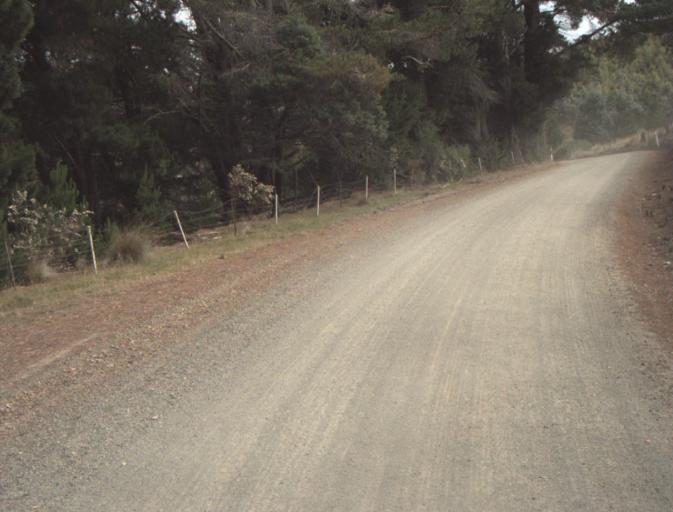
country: AU
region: Tasmania
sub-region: Dorset
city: Scottsdale
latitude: -41.3594
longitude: 147.4606
